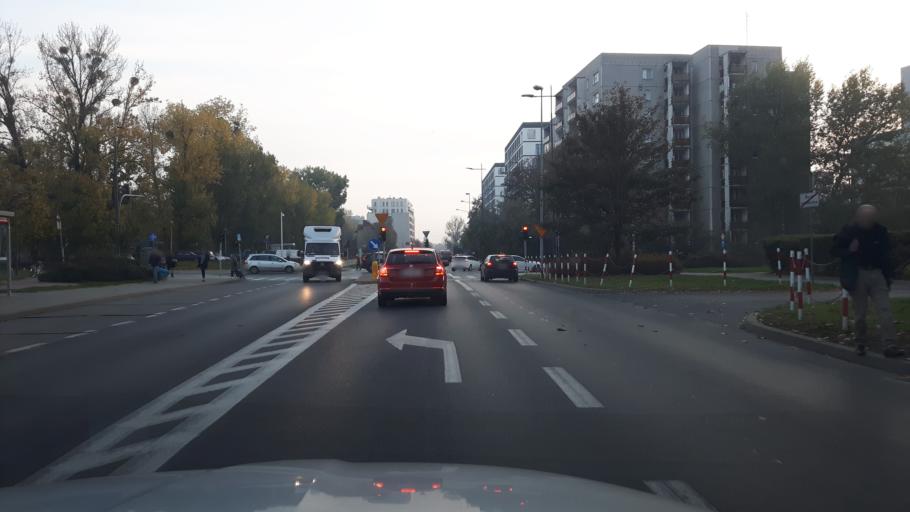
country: PL
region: Masovian Voivodeship
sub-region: Warszawa
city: Mokotow
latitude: 52.1750
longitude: 21.0126
